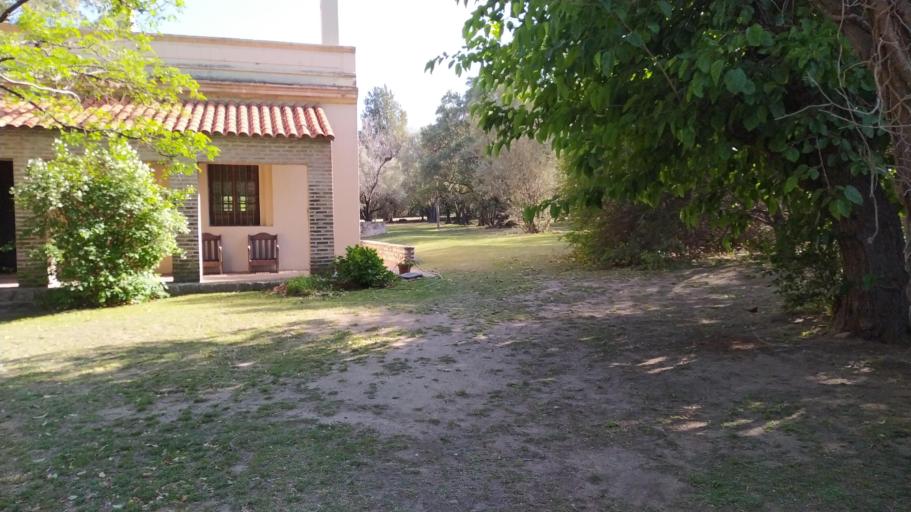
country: AR
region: Cordoba
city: Villa Las Rosas
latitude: -32.0386
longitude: -65.0346
